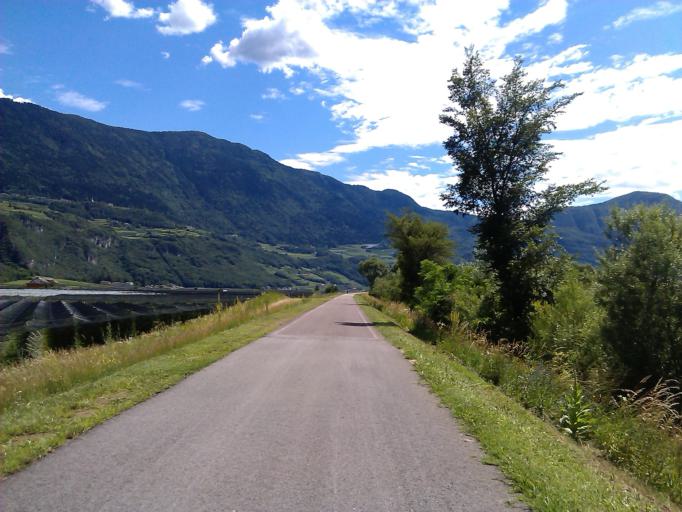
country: IT
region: Trentino-Alto Adige
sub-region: Bolzano
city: Laghetti
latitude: 46.2734
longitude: 11.2351
